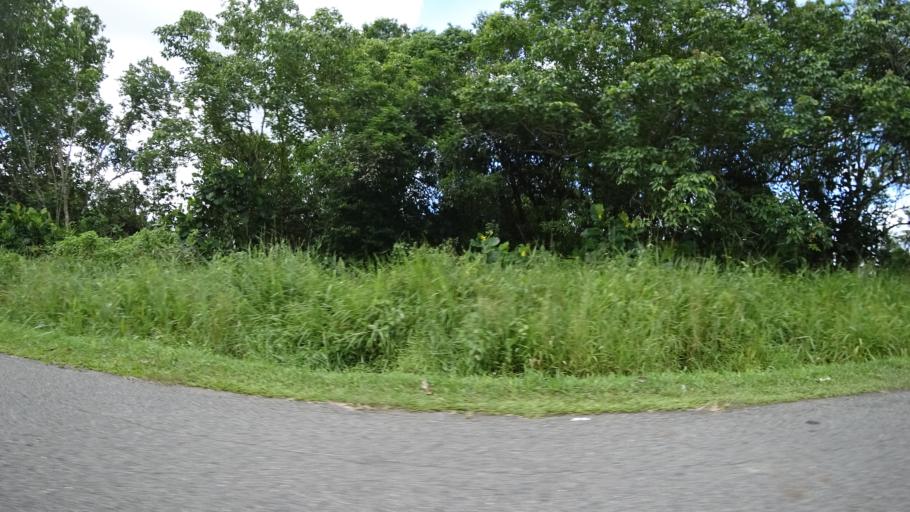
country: MY
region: Sarawak
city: Limbang
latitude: 4.8097
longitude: 114.8542
